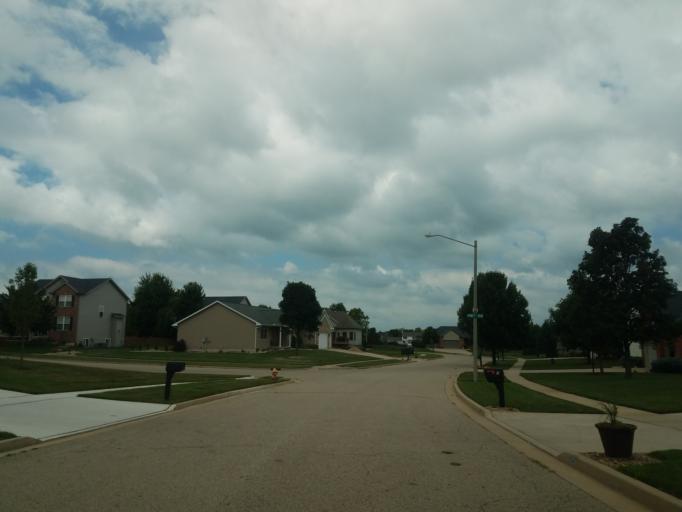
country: US
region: Illinois
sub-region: McLean County
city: Bloomington
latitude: 40.4492
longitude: -89.0373
